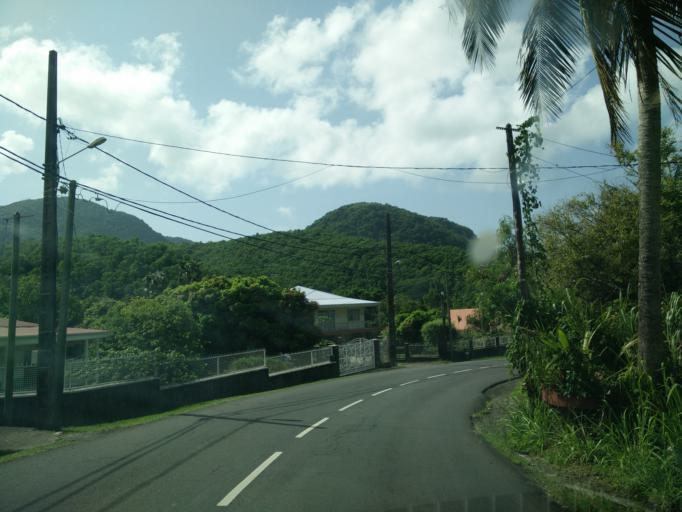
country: GP
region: Guadeloupe
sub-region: Guadeloupe
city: Gourbeyre
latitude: 15.9926
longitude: -61.7057
